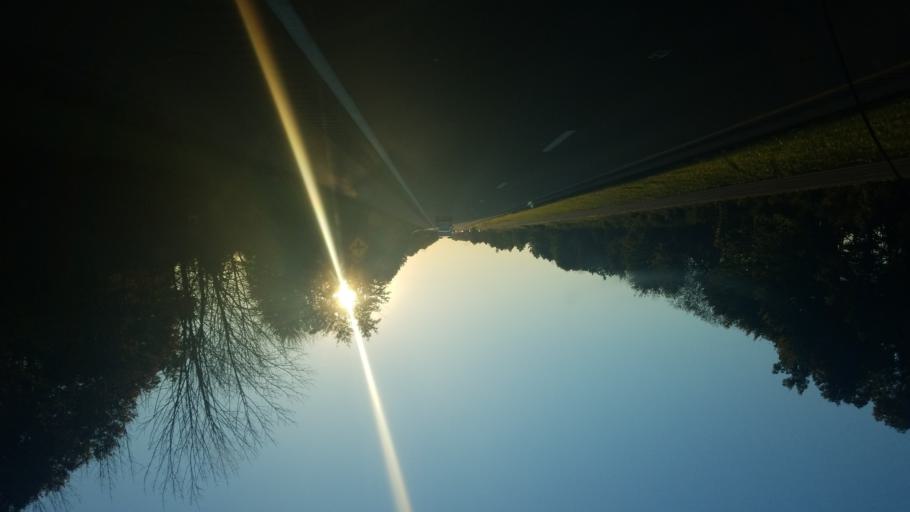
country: US
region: Ohio
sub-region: Stark County
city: Louisville
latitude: 40.8903
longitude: -81.1949
